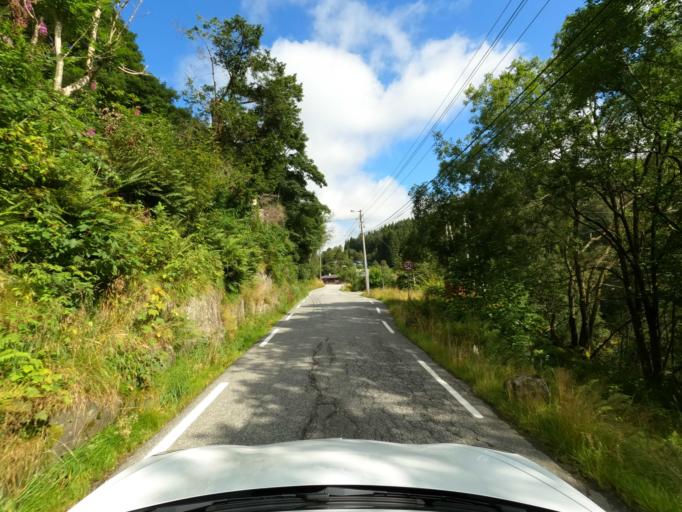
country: NO
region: Hordaland
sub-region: Os
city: Syfteland
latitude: 60.2893
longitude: 5.4313
